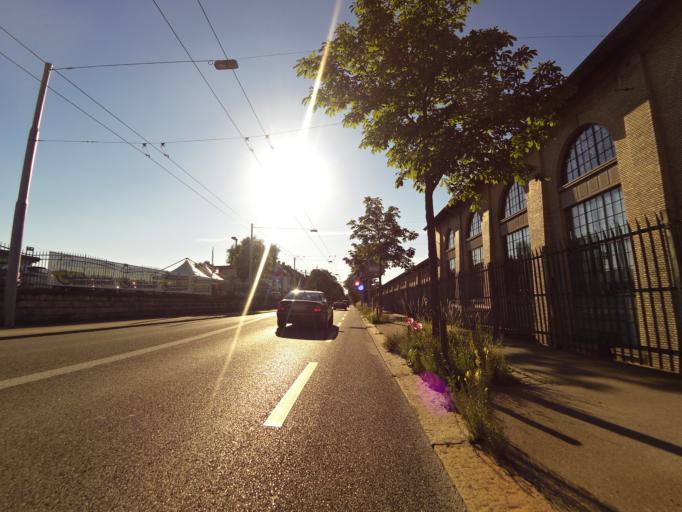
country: CH
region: Zurich
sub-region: Bezirk Zuerich
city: Zuerich (Kreis 4) / Hard
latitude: 47.3858
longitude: 8.5061
